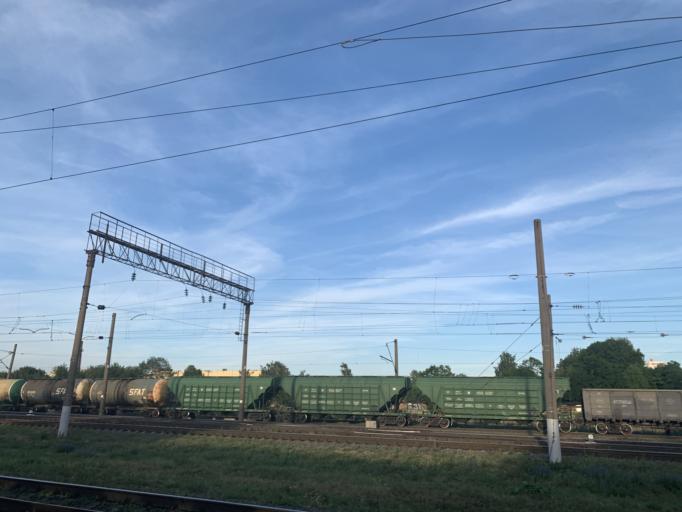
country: BY
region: Minsk
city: Syenitsa
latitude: 53.8590
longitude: 27.5092
